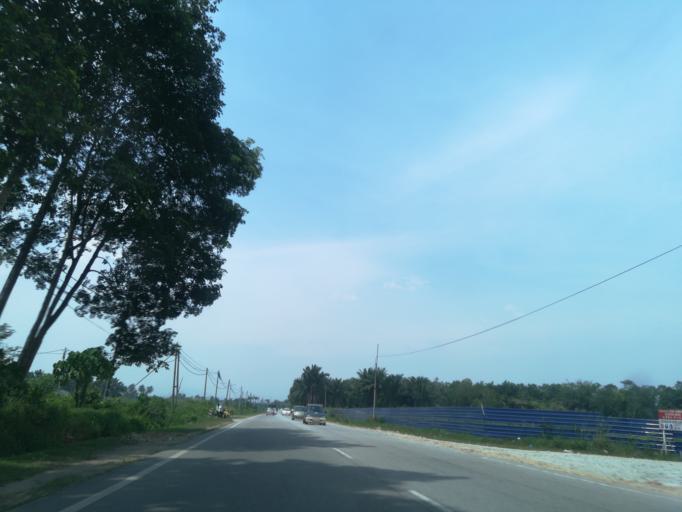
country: MY
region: Penang
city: Tasek Glugor
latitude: 5.4391
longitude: 100.5520
